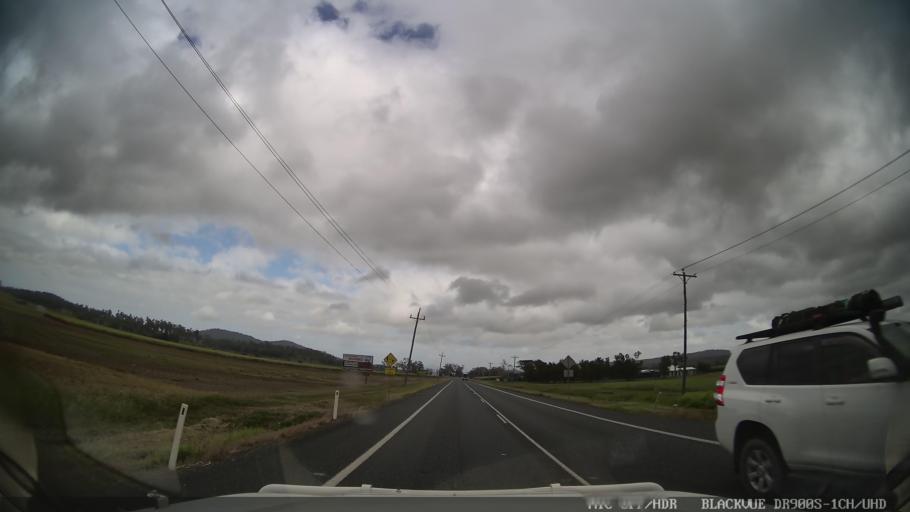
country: AU
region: Queensland
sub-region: Whitsunday
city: Proserpine
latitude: -20.3449
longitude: 148.6297
